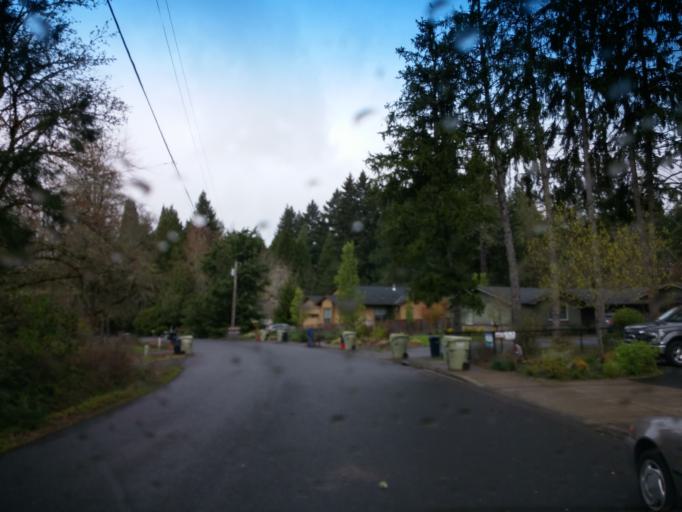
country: US
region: Oregon
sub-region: Washington County
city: Aloha
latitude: 45.5055
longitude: -122.8580
